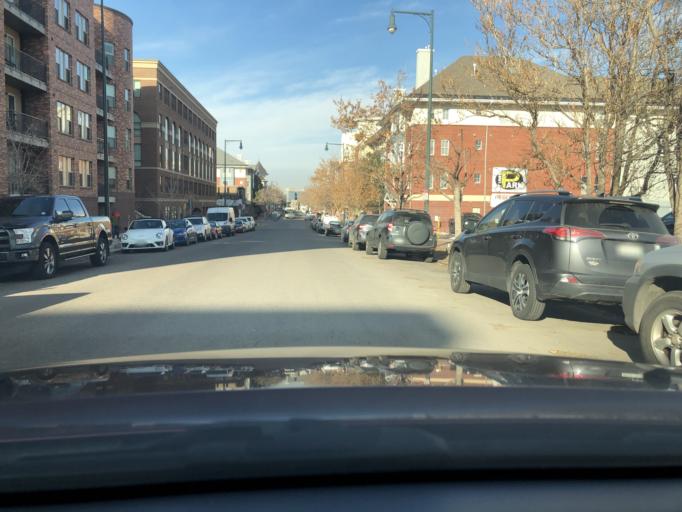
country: US
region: Colorado
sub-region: Denver County
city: Denver
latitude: 39.7450
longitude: -104.9811
